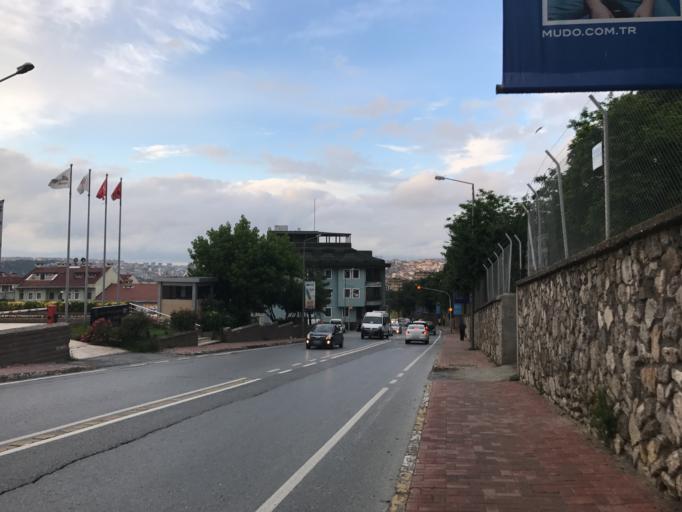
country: TR
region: Istanbul
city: Istanbul
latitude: 41.0332
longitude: 28.9373
